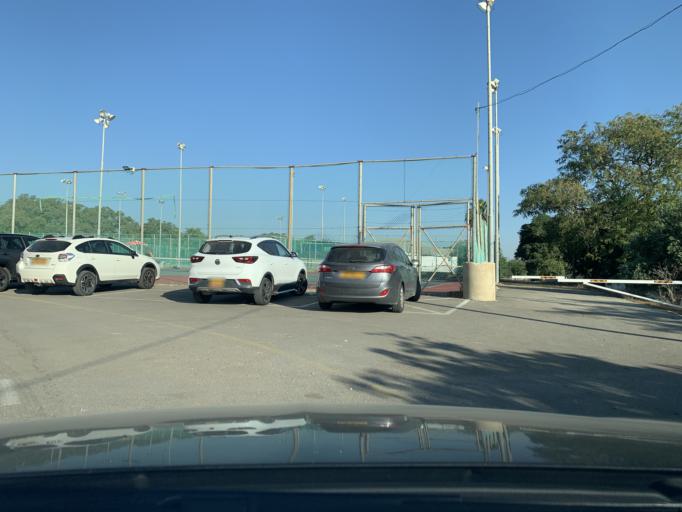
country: IL
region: Central District
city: Rosh Ha'Ayin
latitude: 32.1006
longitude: 34.9239
